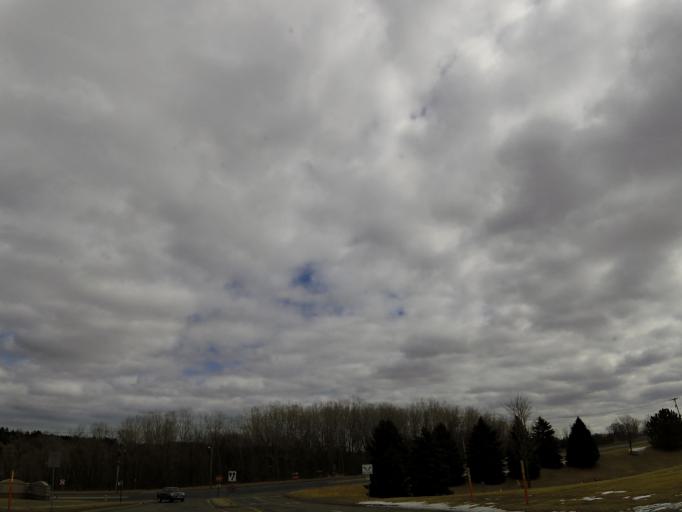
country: US
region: Minnesota
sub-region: Washington County
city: Woodbury
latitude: 44.9281
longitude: -92.9560
